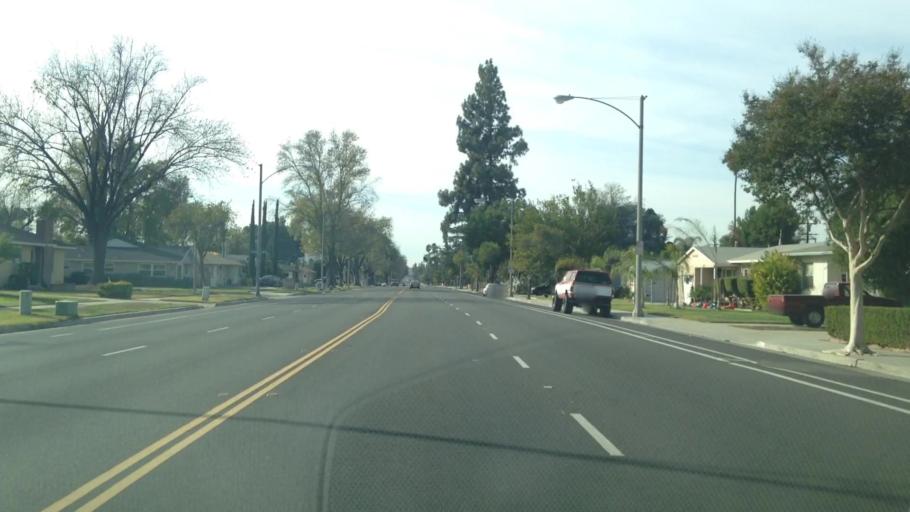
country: US
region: California
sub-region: Riverside County
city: Riverside
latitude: 33.9534
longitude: -117.4073
